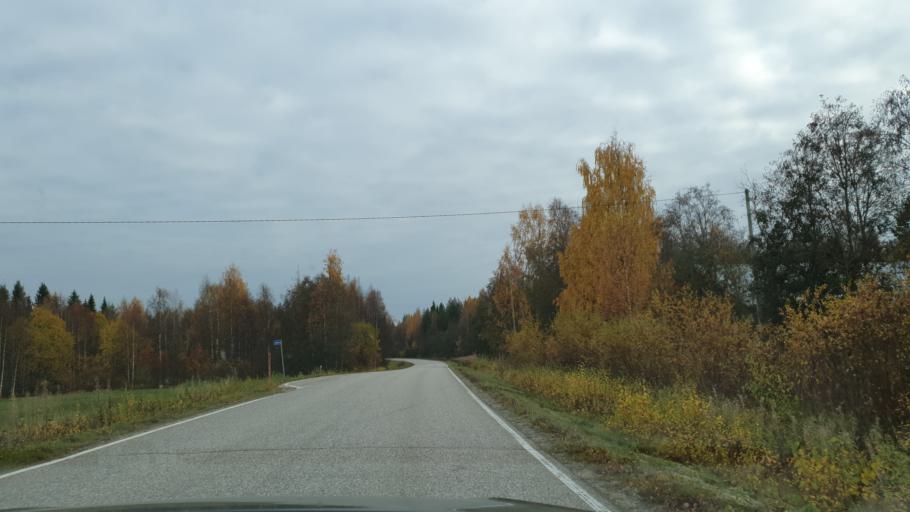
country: FI
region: Kainuu
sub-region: Kajaani
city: Ristijaervi
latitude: 64.4667
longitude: 28.3065
